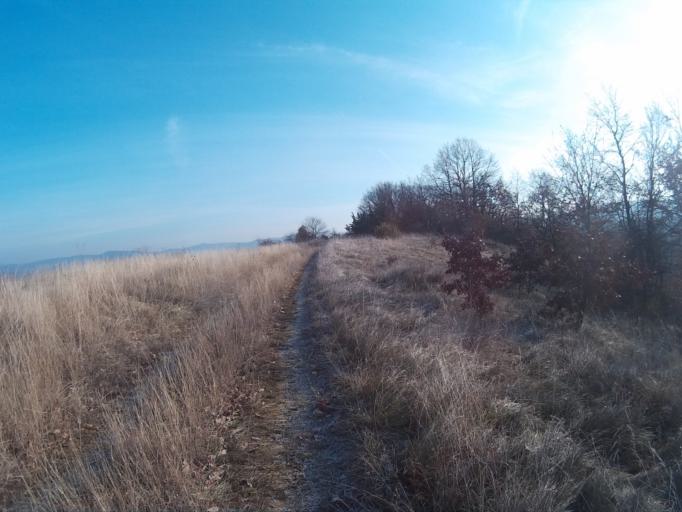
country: HU
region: Nograd
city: Bercel
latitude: 47.9316
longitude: 19.4165
